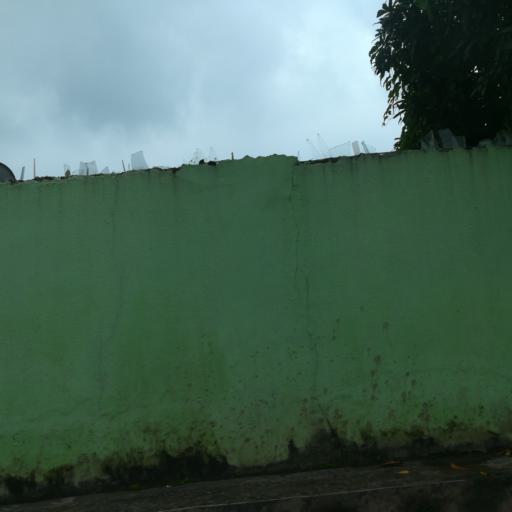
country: NG
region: Lagos
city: Agege
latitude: 6.6007
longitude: 3.3020
